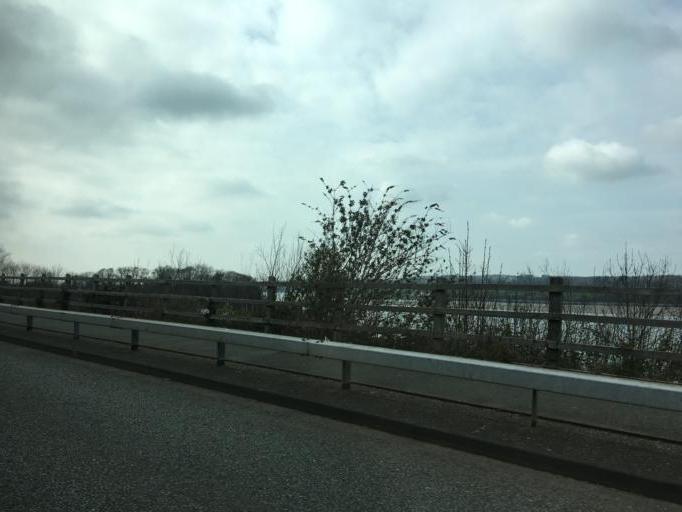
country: GB
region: Wales
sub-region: Gwynedd
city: Y Felinheli
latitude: 53.1817
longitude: -4.2122
